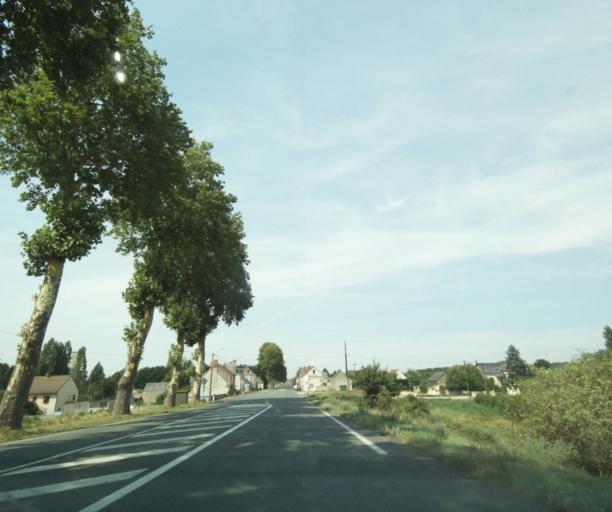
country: FR
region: Centre
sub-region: Departement d'Indre-et-Loire
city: La Celle-Saint-Avant
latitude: 47.0074
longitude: 0.6007
